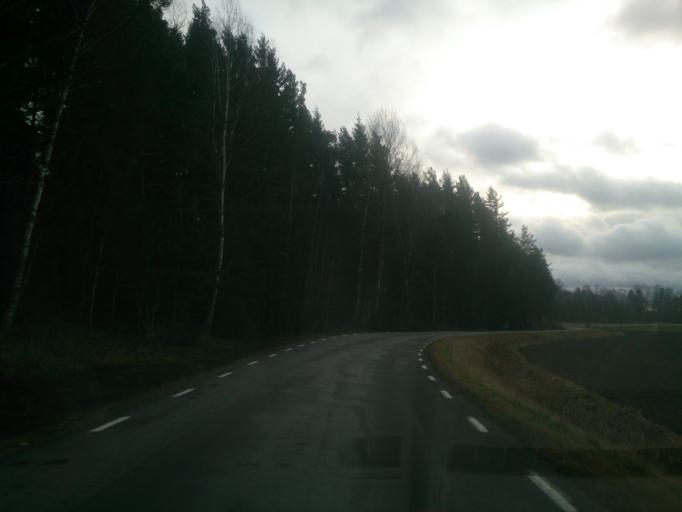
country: SE
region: OEstergoetland
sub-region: Norrkopings Kommun
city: Krokek
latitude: 58.5129
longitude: 16.6020
